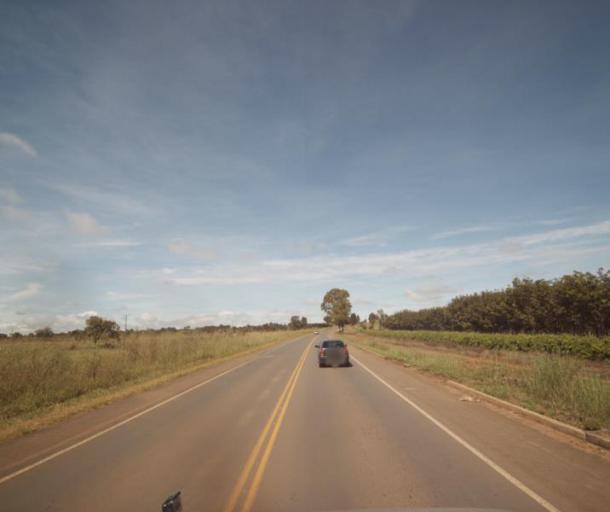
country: BR
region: Goias
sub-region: Anapolis
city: Anapolis
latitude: -16.1992
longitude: -48.9095
